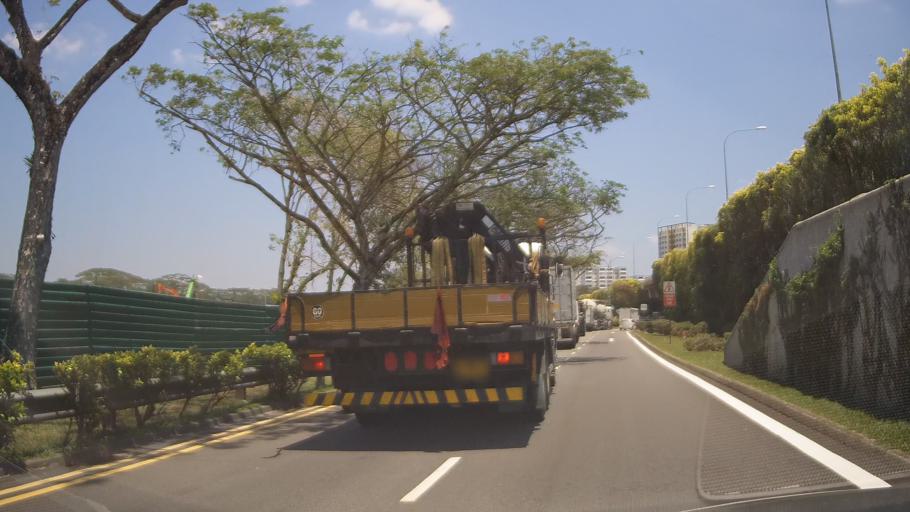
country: MY
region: Johor
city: Johor Bahru
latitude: 1.3566
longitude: 103.7164
